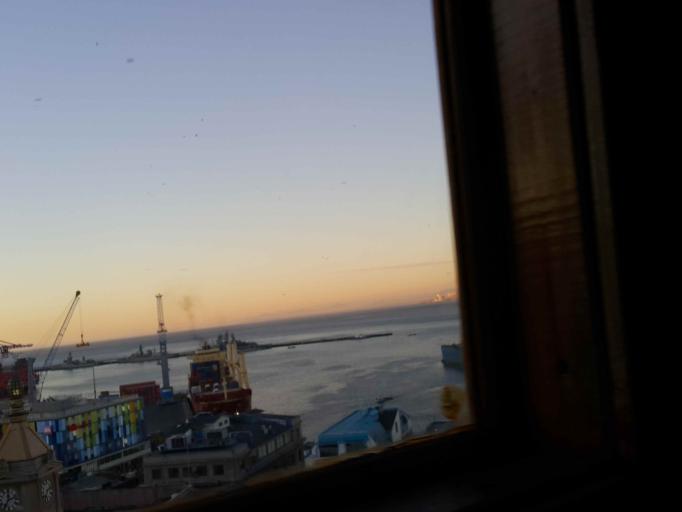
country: CL
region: Valparaiso
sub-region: Provincia de Valparaiso
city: Valparaiso
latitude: -33.0412
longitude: -71.6263
